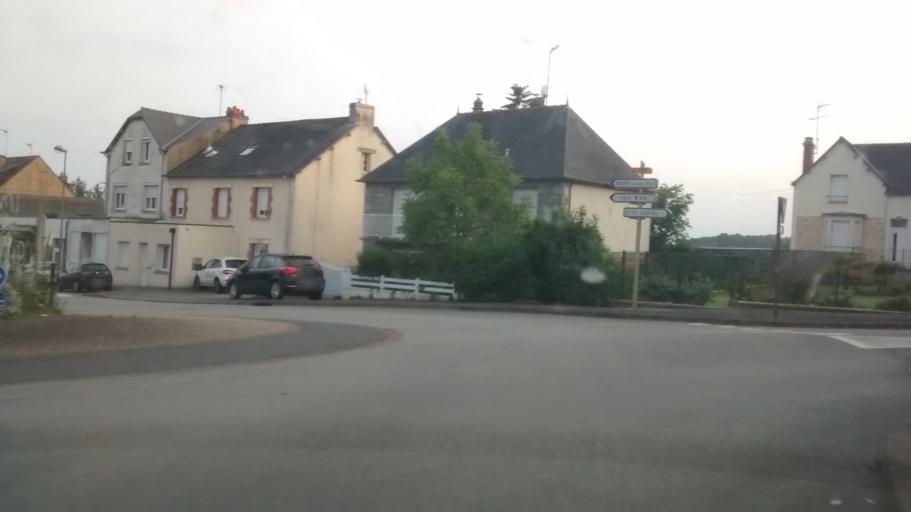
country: FR
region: Brittany
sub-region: Departement du Morbihan
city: Guer
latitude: 47.9402
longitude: -2.1333
